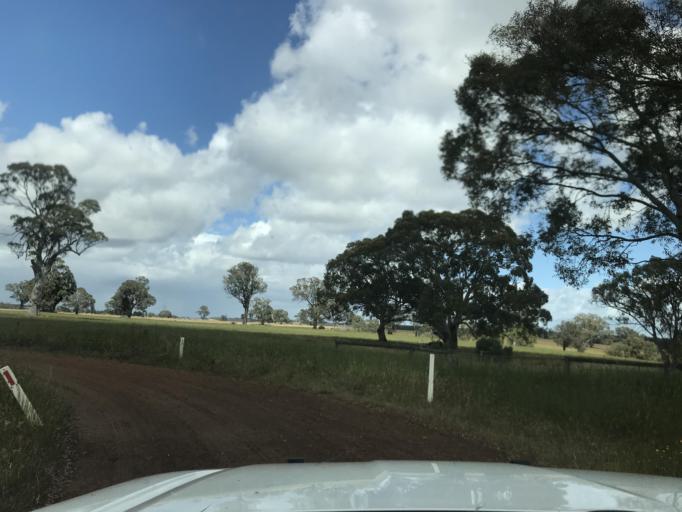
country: AU
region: South Australia
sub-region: Wattle Range
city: Penola
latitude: -37.1938
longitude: 141.4180
